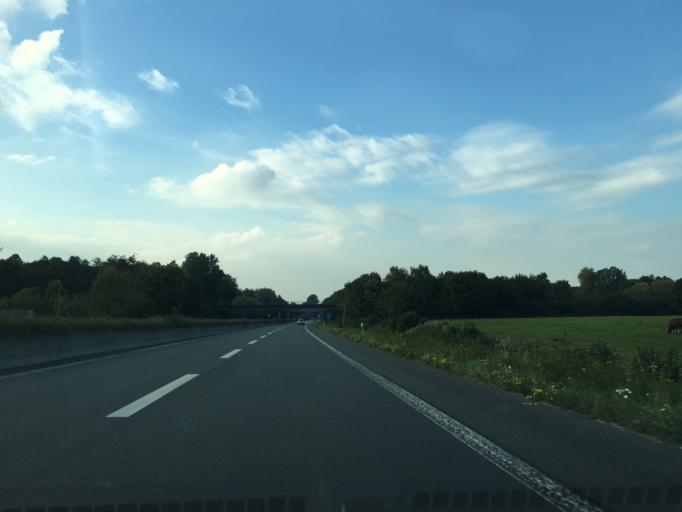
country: DE
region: North Rhine-Westphalia
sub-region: Regierungsbezirk Munster
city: Dulmen
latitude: 51.8480
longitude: 7.2904
